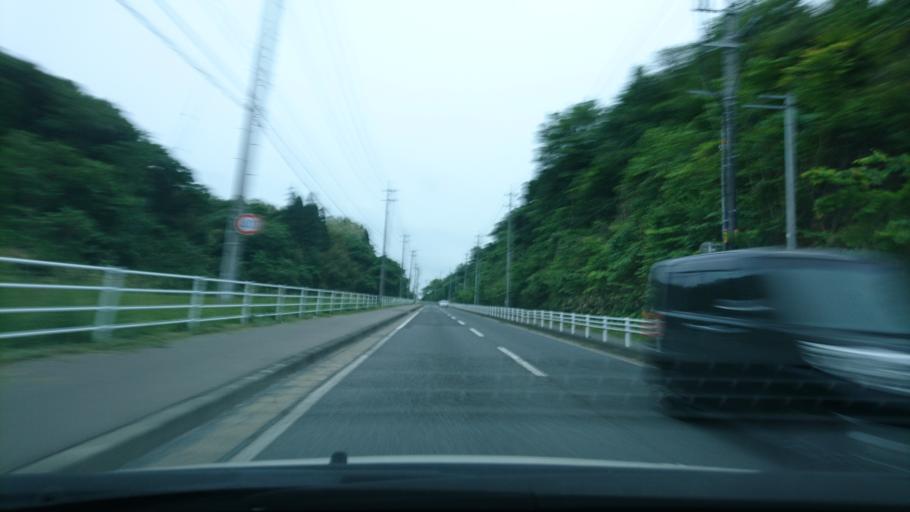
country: JP
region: Iwate
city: Ichinoseki
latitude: 38.9215
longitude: 141.1485
